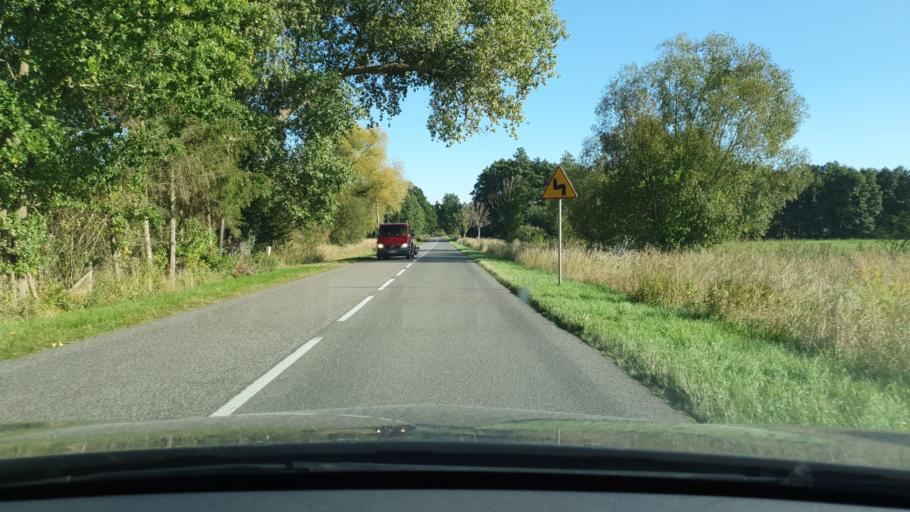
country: PL
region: West Pomeranian Voivodeship
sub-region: Powiat goleniowski
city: Przybiernow
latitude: 53.8305
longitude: 14.7749
